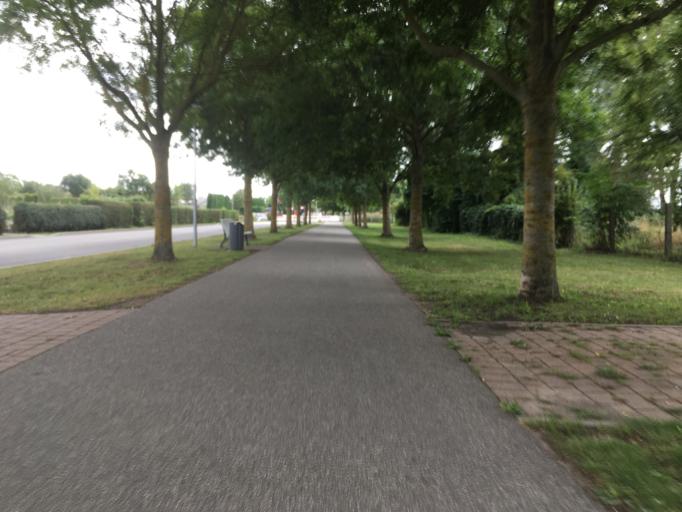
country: DE
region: Brandenburg
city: Prenzlau
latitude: 53.3017
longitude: 13.8639
